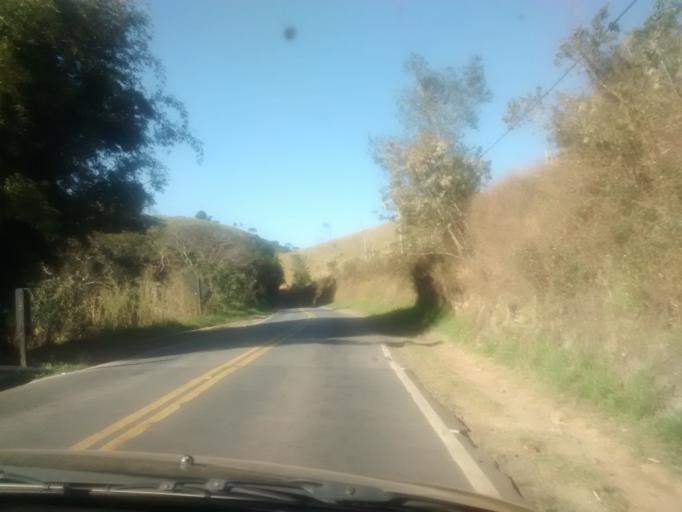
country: BR
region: Sao Paulo
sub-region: Campos Do Jordao
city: Campos do Jordao
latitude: -22.8243
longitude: -45.7340
